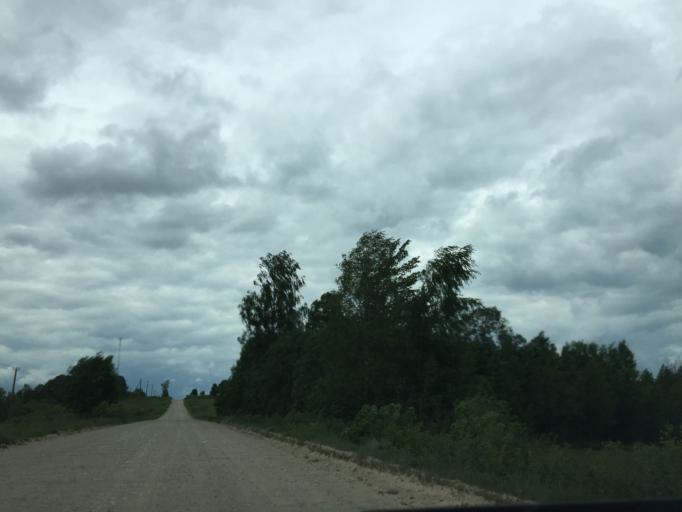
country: LV
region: Dagda
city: Dagda
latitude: 56.0104
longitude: 27.6026
